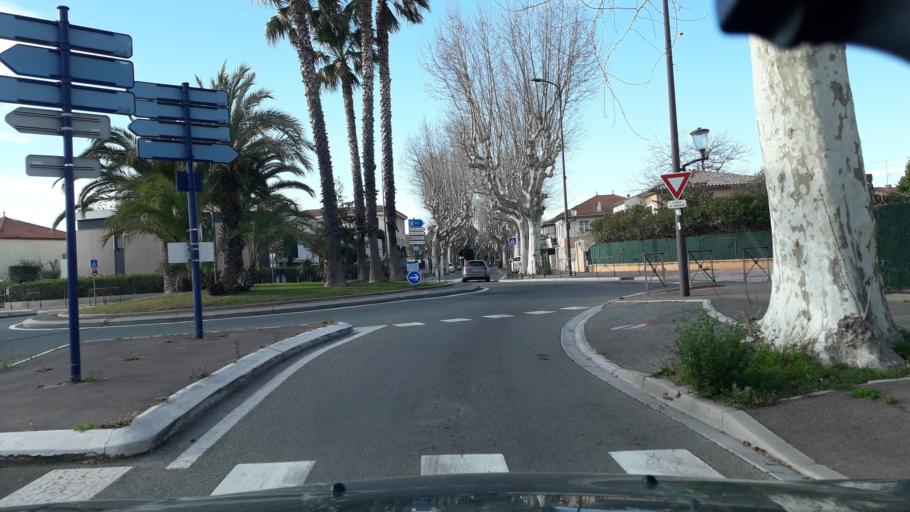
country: FR
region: Provence-Alpes-Cote d'Azur
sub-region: Departement du Var
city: Frejus
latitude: 43.4254
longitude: 6.7389
